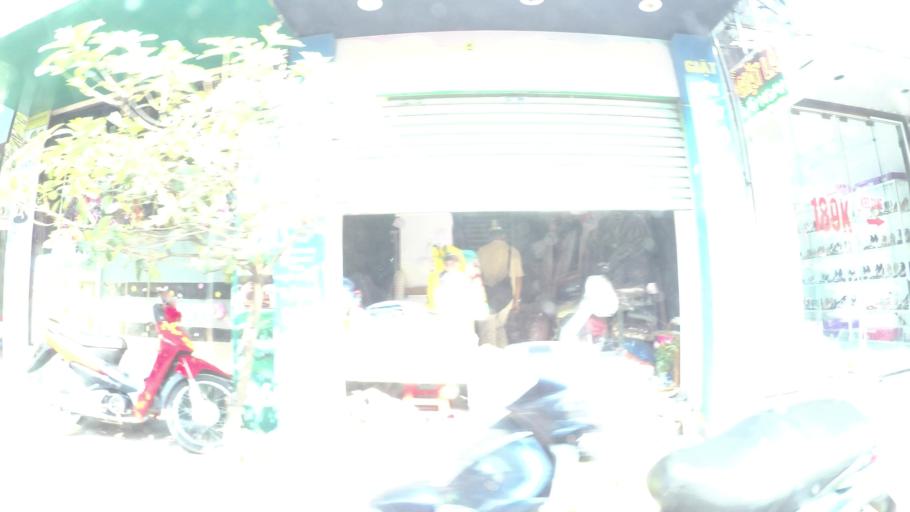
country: VN
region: Ha Noi
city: Thanh Xuan
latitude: 20.9951
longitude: 105.8175
